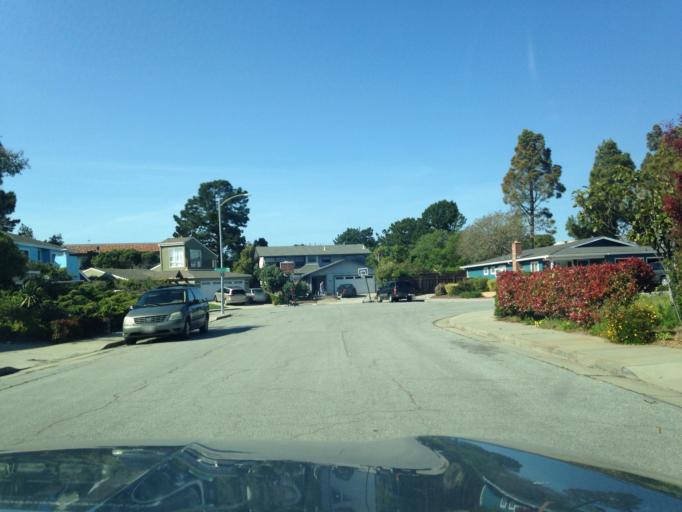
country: US
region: California
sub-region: Santa Cruz County
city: Santa Cruz
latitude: 36.9532
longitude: -122.0532
